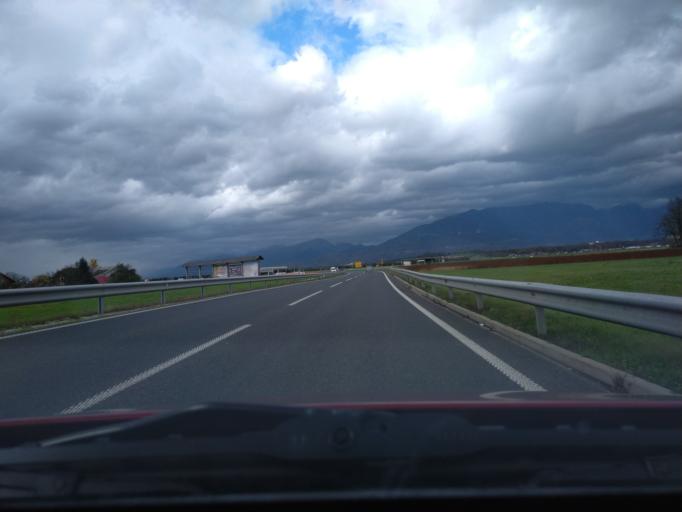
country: SI
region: Menges
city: Menges
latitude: 46.1706
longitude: 14.5798
